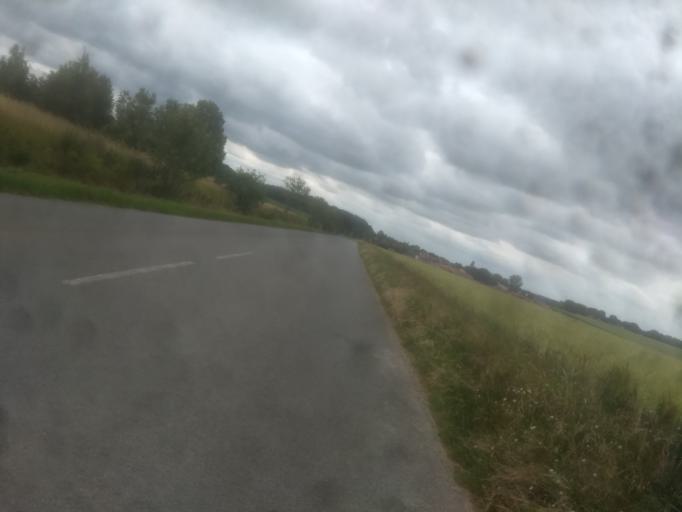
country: FR
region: Nord-Pas-de-Calais
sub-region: Departement du Pas-de-Calais
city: Thelus
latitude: 50.3346
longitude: 2.7941
